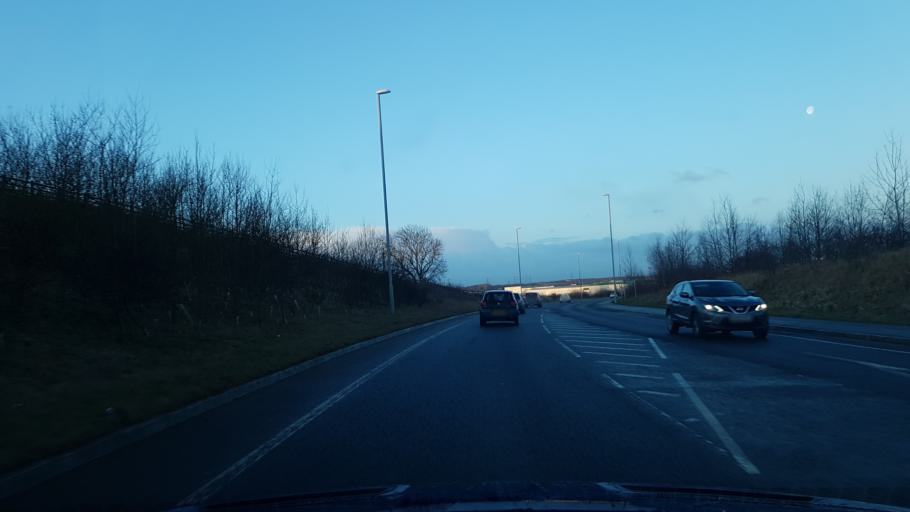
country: GB
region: England
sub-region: City and Borough of Wakefield
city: Castleford
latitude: 53.7032
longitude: -1.3705
